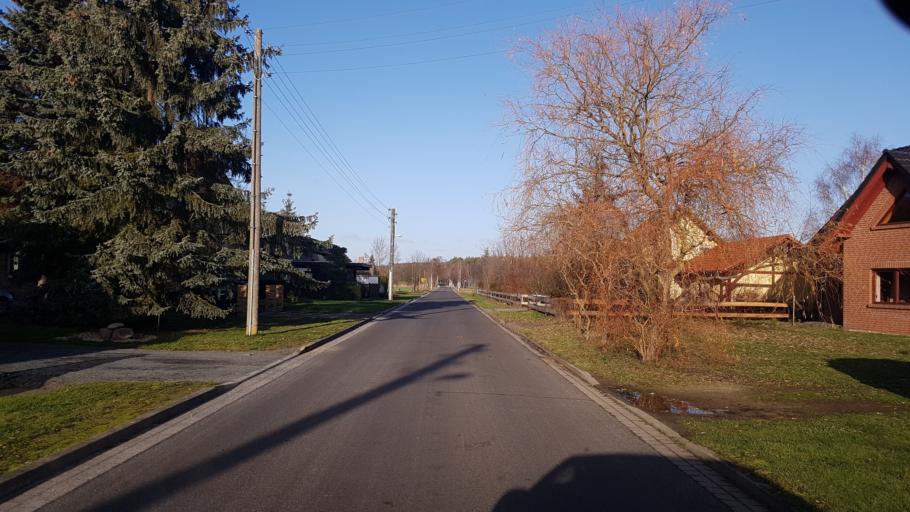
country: DE
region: Brandenburg
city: Ruckersdorf
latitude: 51.5970
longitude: 13.6076
